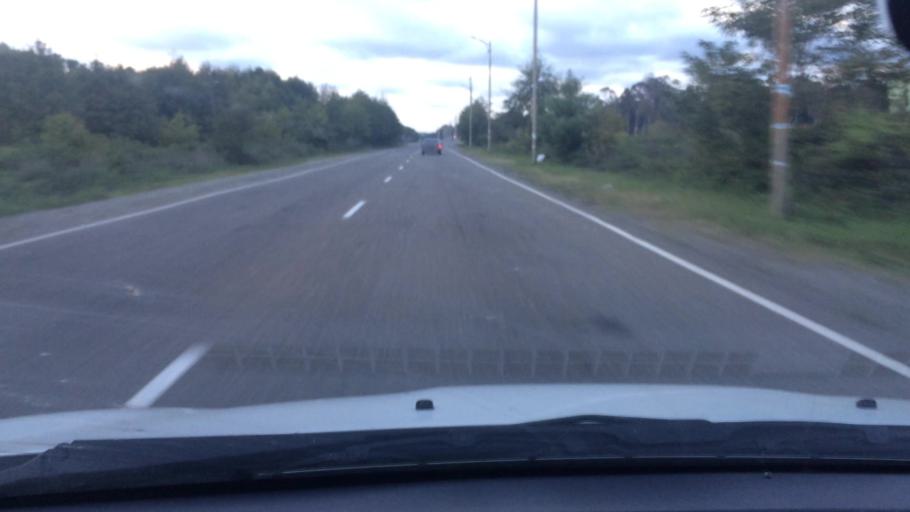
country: GE
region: Guria
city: Urek'i
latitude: 41.9348
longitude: 41.7720
